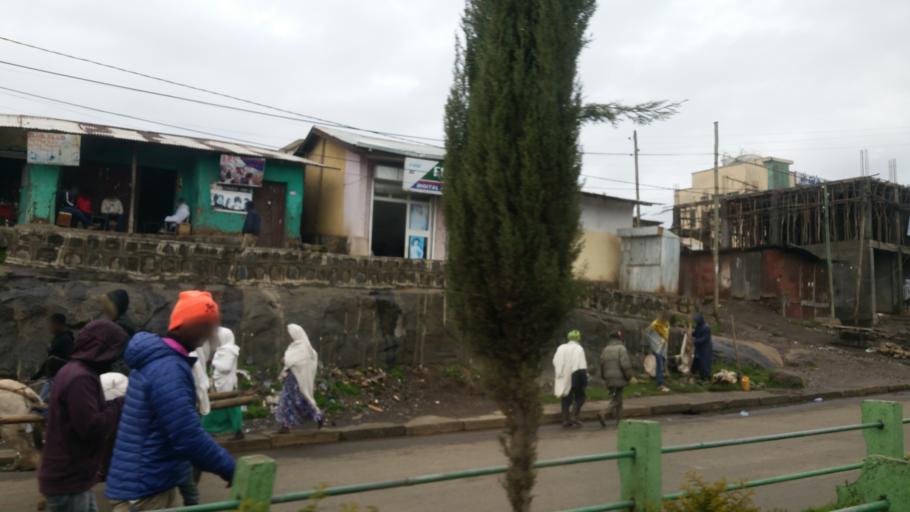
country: ET
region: Amhara
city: Debark'
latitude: 13.1564
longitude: 37.8983
